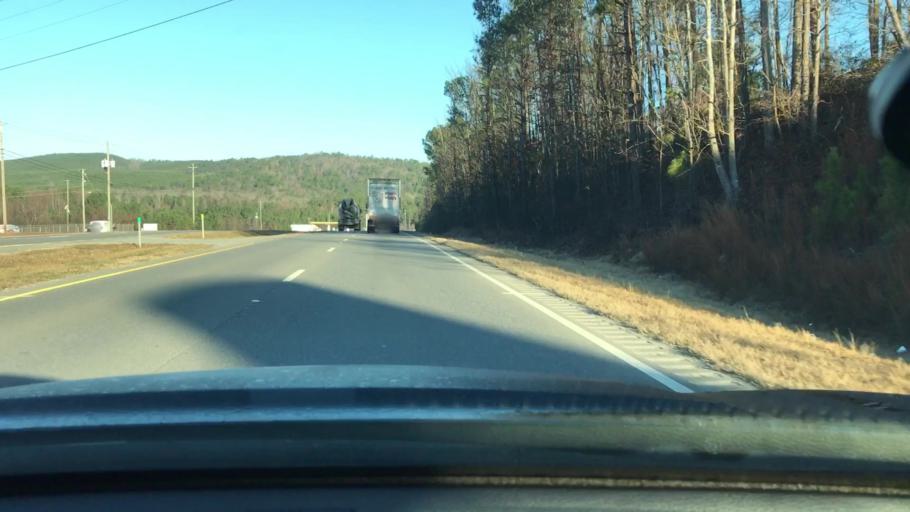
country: US
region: Alabama
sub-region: Talladega County
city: Mignon
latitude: 33.1893
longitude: -86.3052
